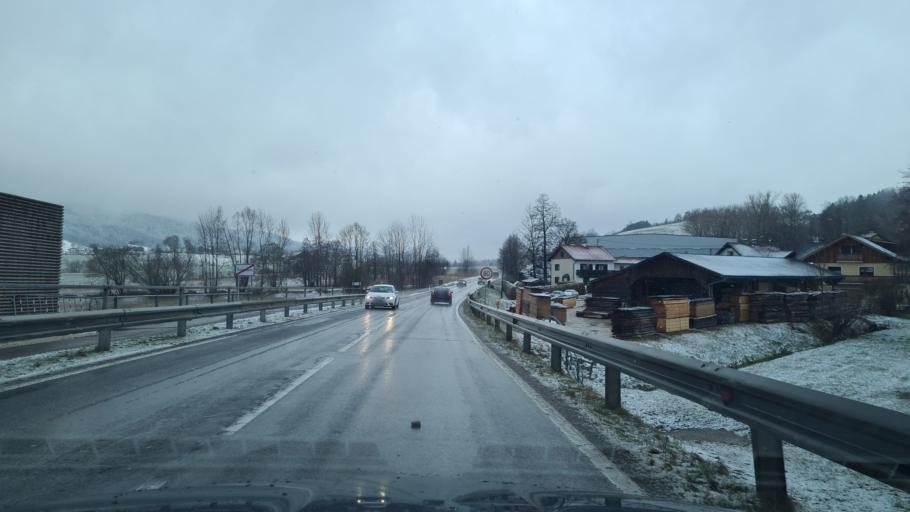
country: AT
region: Upper Austria
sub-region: Politischer Bezirk Vocklabruck
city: Zell am Moos
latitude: 47.8739
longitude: 13.3217
